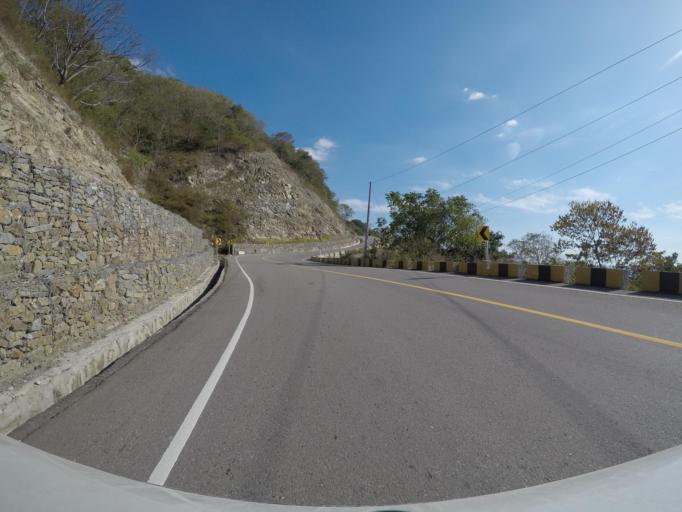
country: TL
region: Liquica
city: Maubara
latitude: -8.6491
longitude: 125.1222
